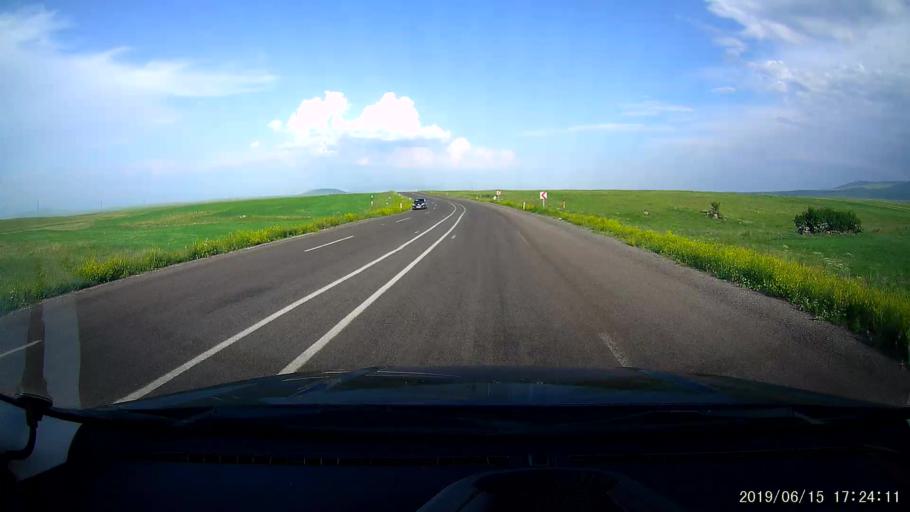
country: TR
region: Kars
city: Basgedikler
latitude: 40.6152
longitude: 43.3782
